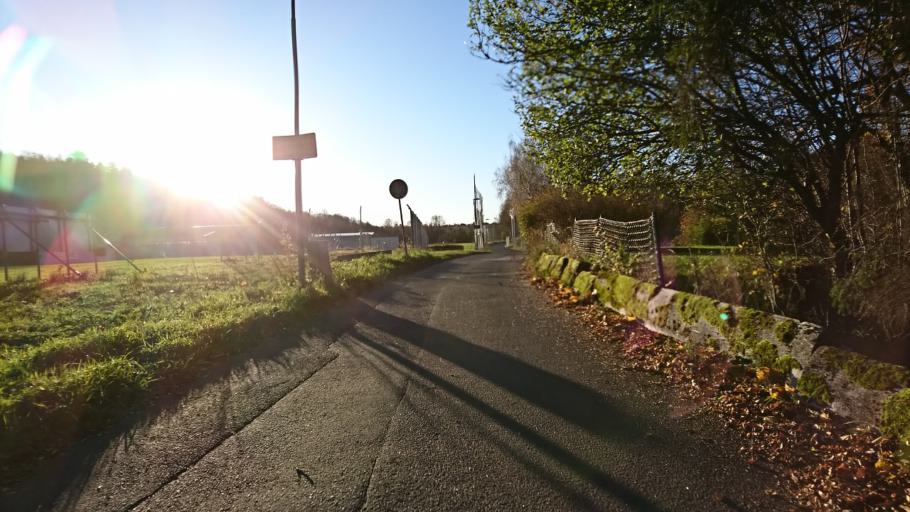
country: SE
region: Vaestra Goetaland
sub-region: Molndal
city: Moelndal
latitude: 57.6813
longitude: 12.0233
